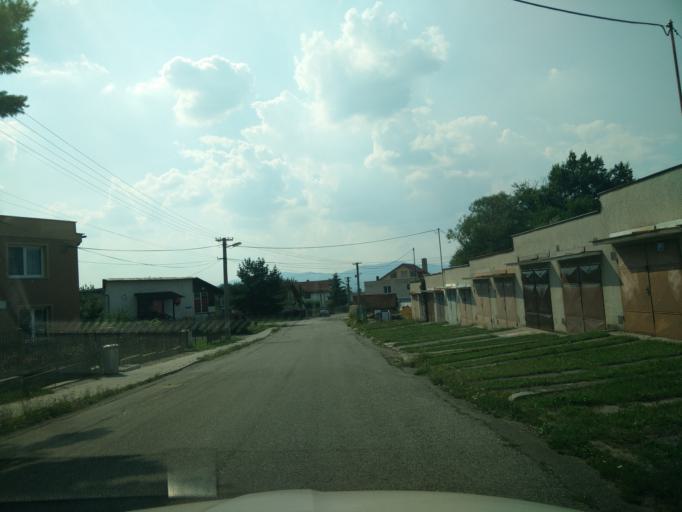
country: SK
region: Nitriansky
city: Prievidza
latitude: 48.7307
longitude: 18.6276
